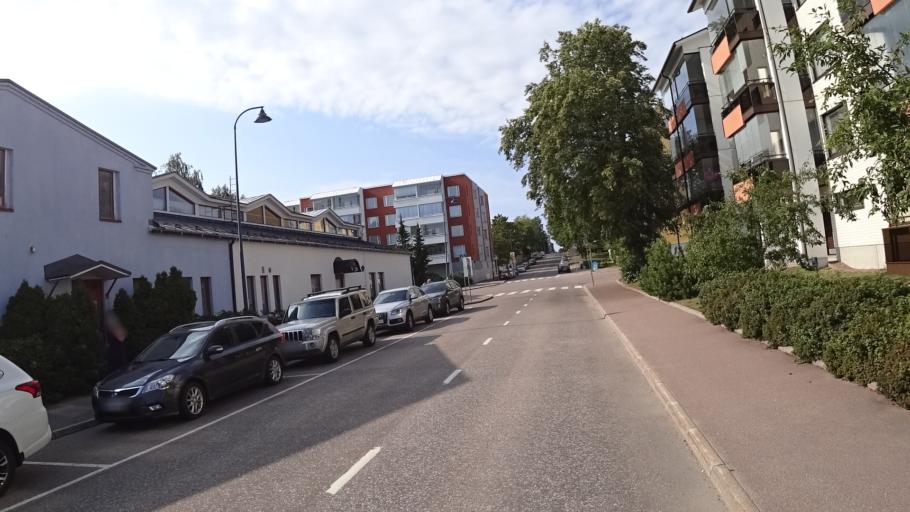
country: FI
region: Kymenlaakso
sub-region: Kotka-Hamina
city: Kotka
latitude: 60.4618
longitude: 26.9504
